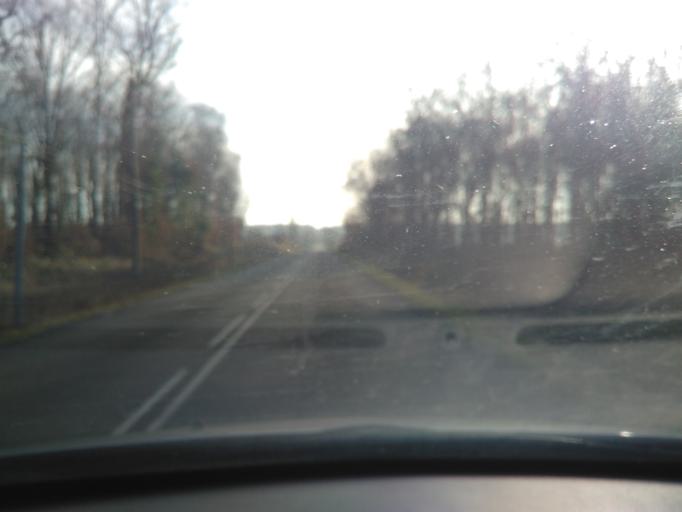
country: FR
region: Bourgogne
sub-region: Departement de la Nievre
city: Dornes
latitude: 46.7828
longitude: 3.2774
